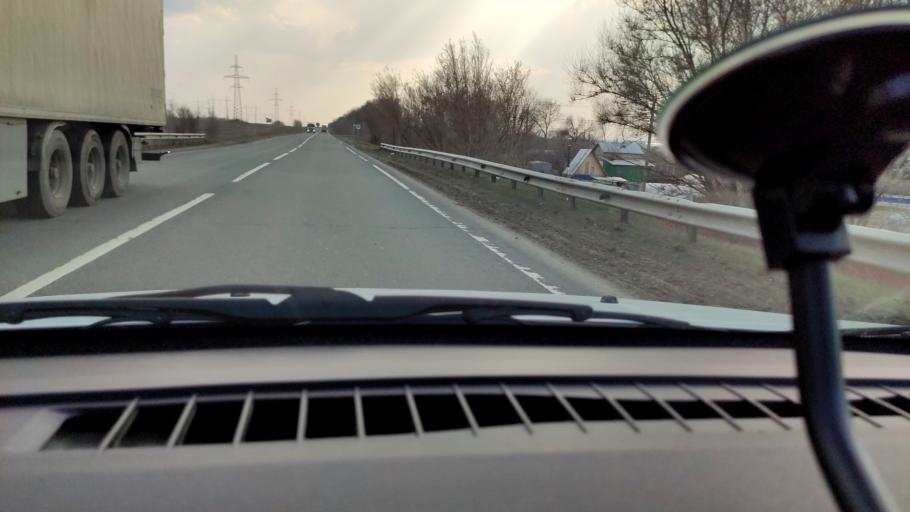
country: RU
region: Samara
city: Dubovyy Umet
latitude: 53.0834
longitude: 50.3917
